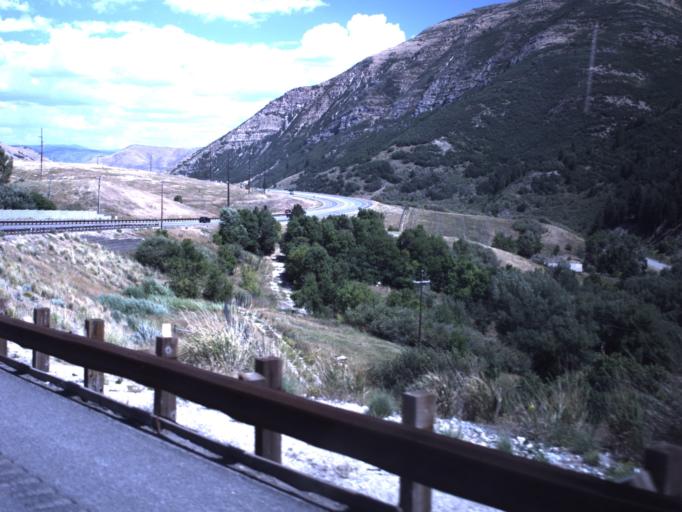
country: US
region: Utah
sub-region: Wasatch County
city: Midway
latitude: 40.3894
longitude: -111.5482
